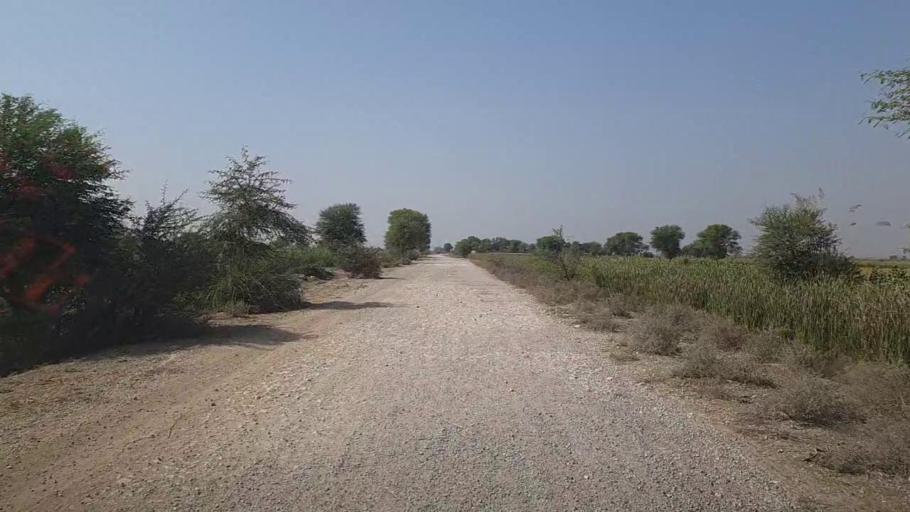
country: PK
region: Sindh
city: Kandhkot
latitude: 28.3933
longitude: 69.2790
